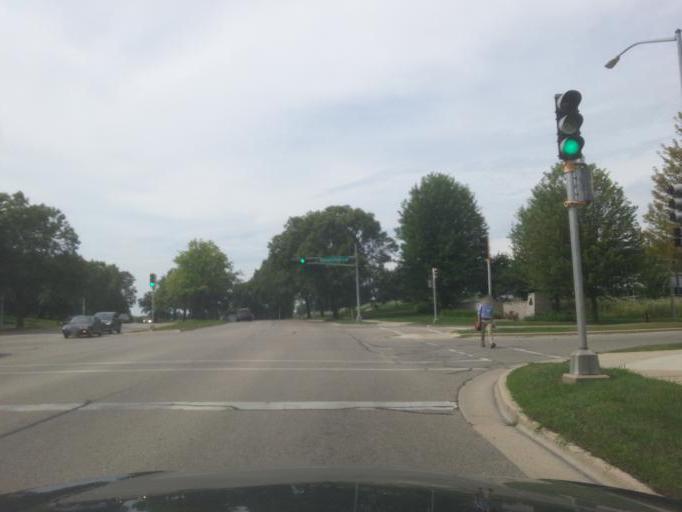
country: US
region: Wisconsin
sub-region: Dane County
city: Shorewood Hills
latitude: 43.0564
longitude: -89.4732
